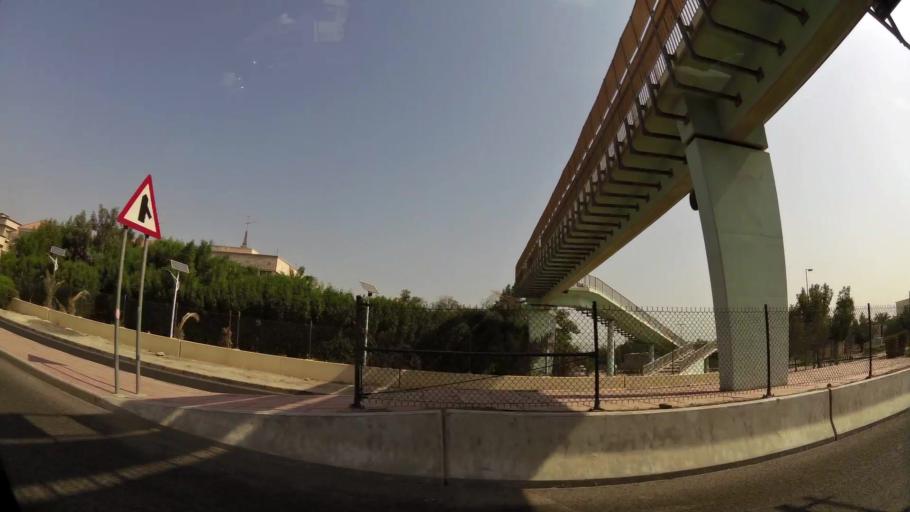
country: KW
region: Al Asimah
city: Ad Dasmah
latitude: 29.3571
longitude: 47.9898
